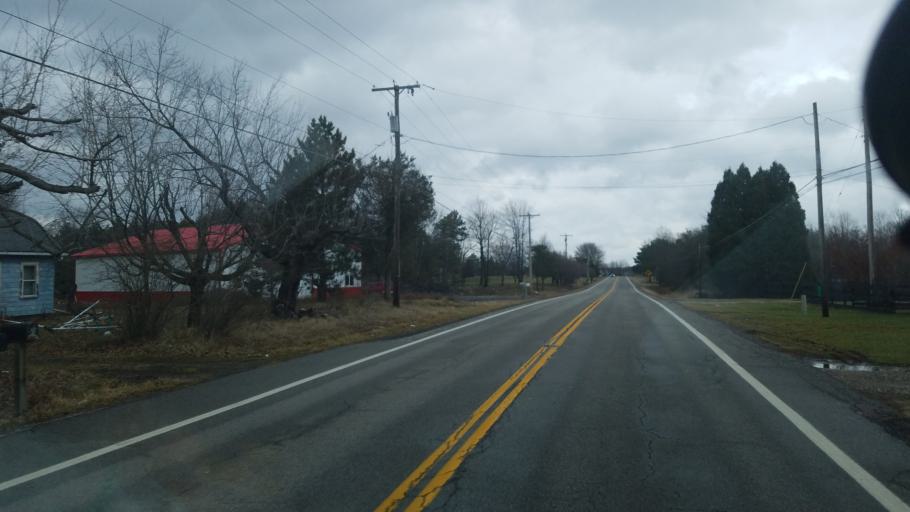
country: US
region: Ohio
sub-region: Crawford County
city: Crestline
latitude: 40.7647
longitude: -82.6803
